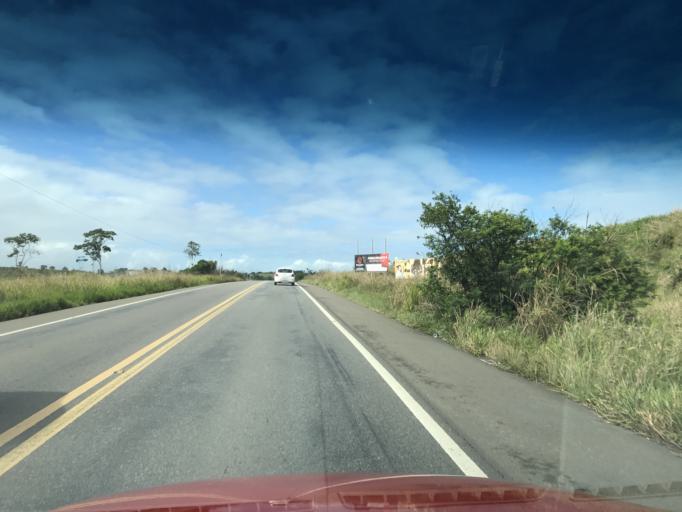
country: BR
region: Bahia
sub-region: Conceicao Do Almeida
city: Muritiba
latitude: -12.9369
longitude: -39.2523
